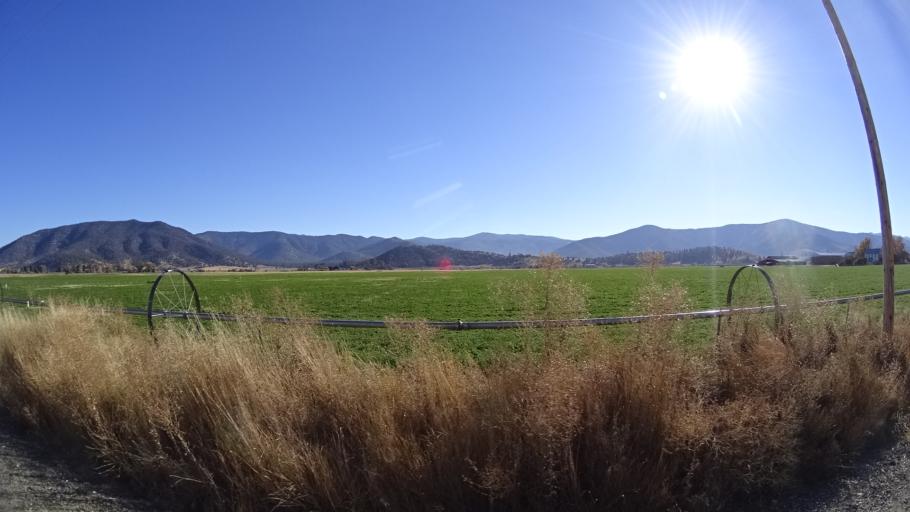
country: US
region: California
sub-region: Siskiyou County
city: Yreka
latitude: 41.4940
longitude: -122.8594
